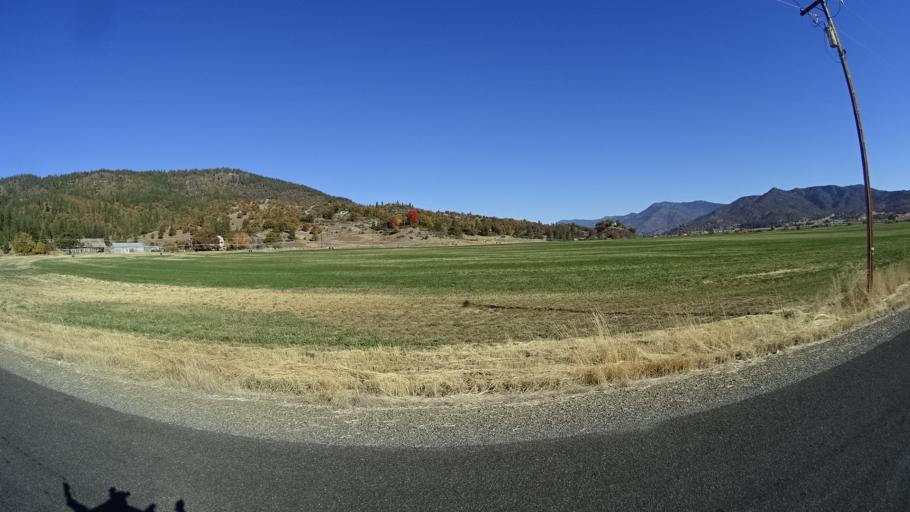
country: US
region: California
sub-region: Siskiyou County
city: Yreka
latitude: 41.5776
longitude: -122.8643
